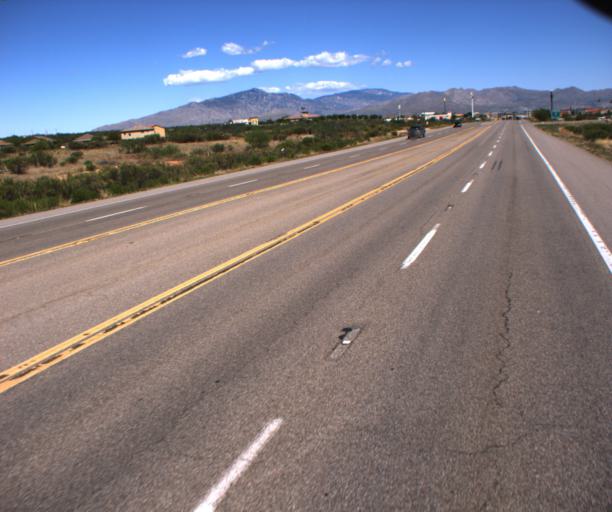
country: US
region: Arizona
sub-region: Cochise County
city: Whetstone
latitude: 31.9565
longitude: -110.3431
